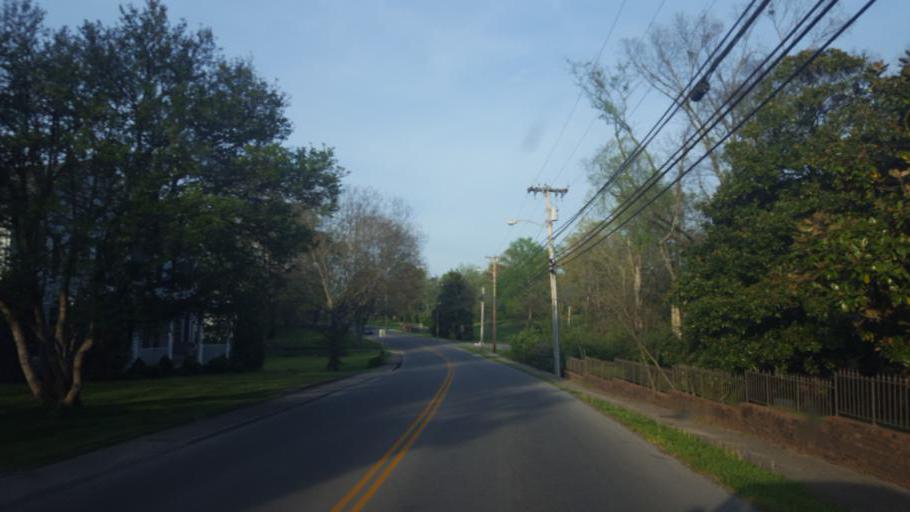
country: US
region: Kentucky
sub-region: Barren County
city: Glasgow
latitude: 36.9872
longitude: -85.9211
